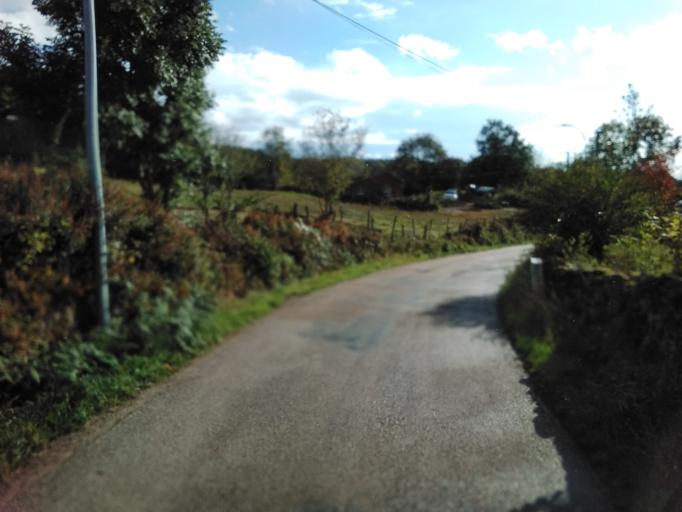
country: FR
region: Bourgogne
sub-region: Departement de la Nievre
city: Lormes
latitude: 47.2921
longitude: 3.8574
